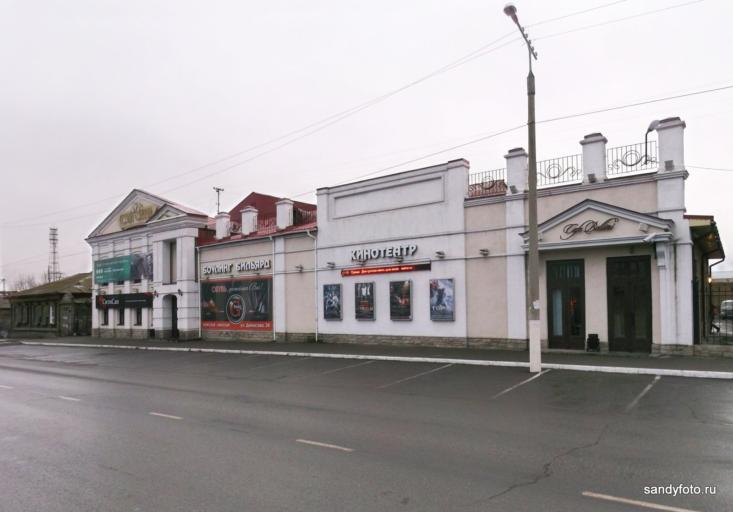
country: RU
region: Chelyabinsk
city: Troitsk
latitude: 54.0834
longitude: 61.5512
